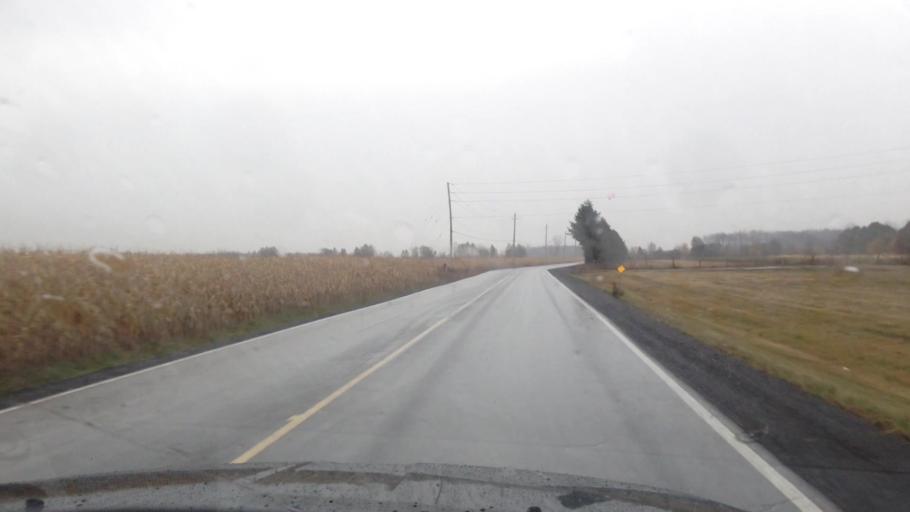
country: CA
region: Ontario
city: Bourget
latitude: 45.2959
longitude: -75.2605
